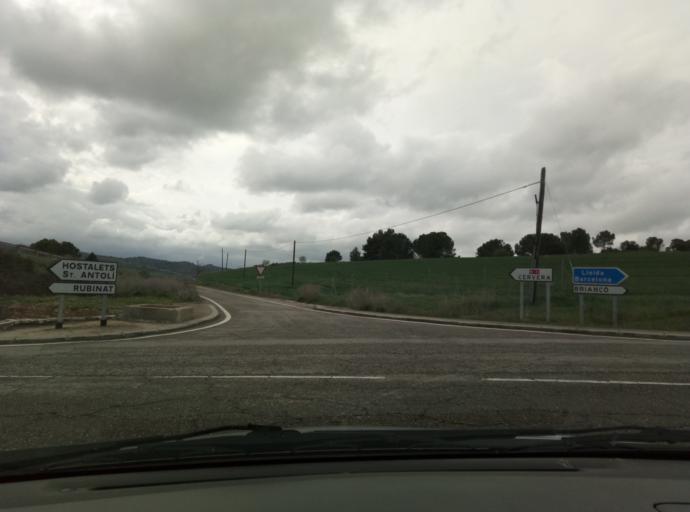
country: ES
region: Catalonia
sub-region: Provincia de Lleida
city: Cervera
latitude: 41.6332
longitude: 1.3393
